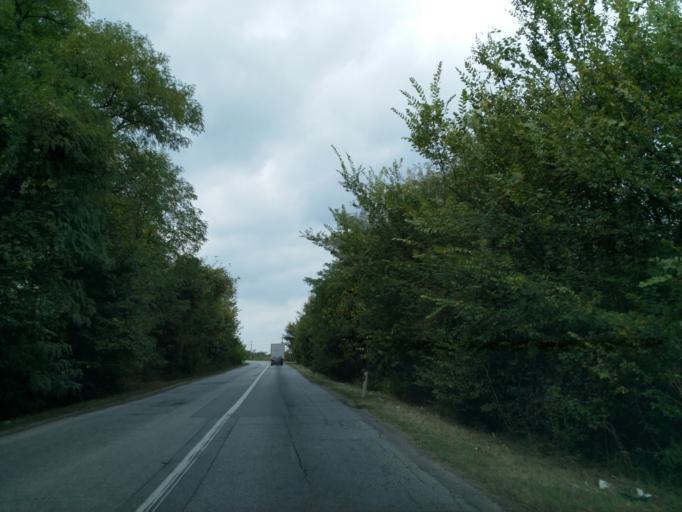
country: RS
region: Central Serbia
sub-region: Sumadijski Okrug
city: Topola
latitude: 44.1351
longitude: 20.7946
